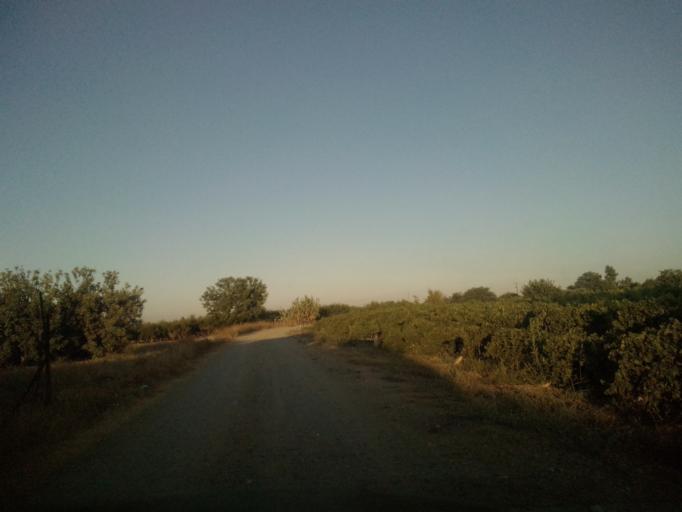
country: CY
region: Limassol
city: Ypsonas
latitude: 34.6744
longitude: 32.9666
